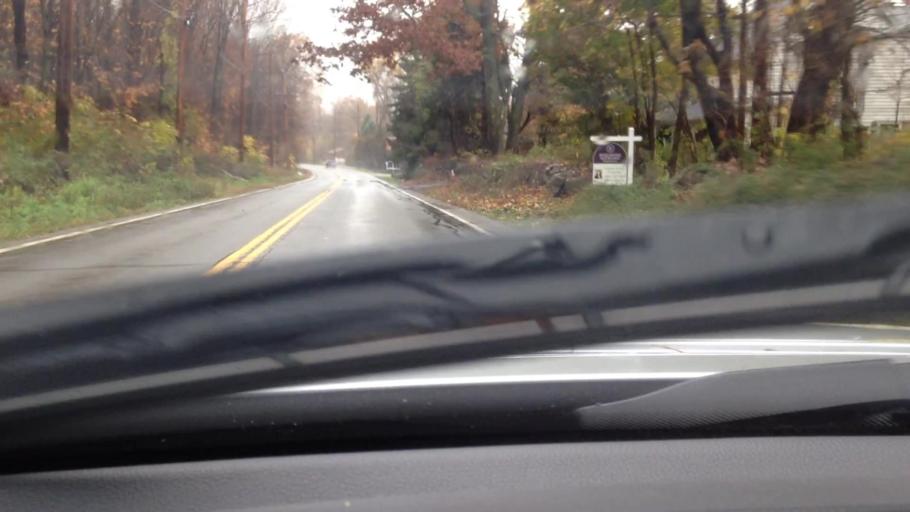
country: US
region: New York
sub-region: Orange County
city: Cornwall-on-Hudson
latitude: 41.4614
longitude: -73.9804
